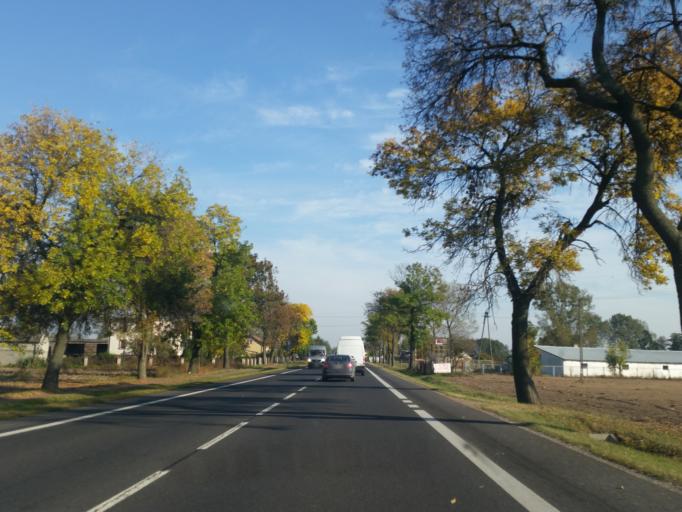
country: PL
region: Masovian Voivodeship
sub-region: Powiat sierpecki
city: Zawidz
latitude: 52.8115
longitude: 19.8130
